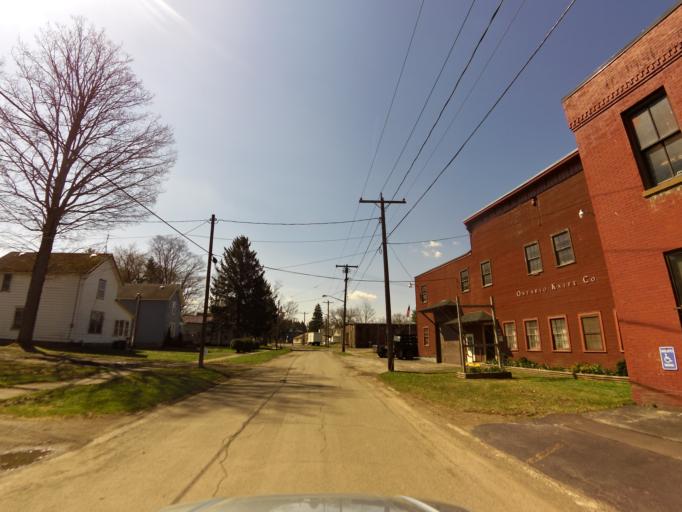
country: US
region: New York
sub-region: Cattaraugus County
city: Franklinville
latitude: 42.3391
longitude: -78.4601
